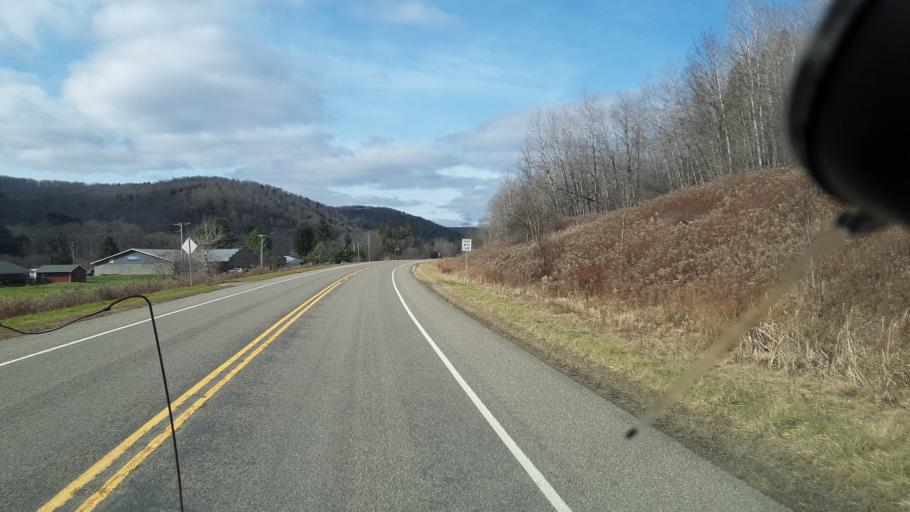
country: US
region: Pennsylvania
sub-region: Potter County
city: Galeton
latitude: 41.7776
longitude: -77.7230
